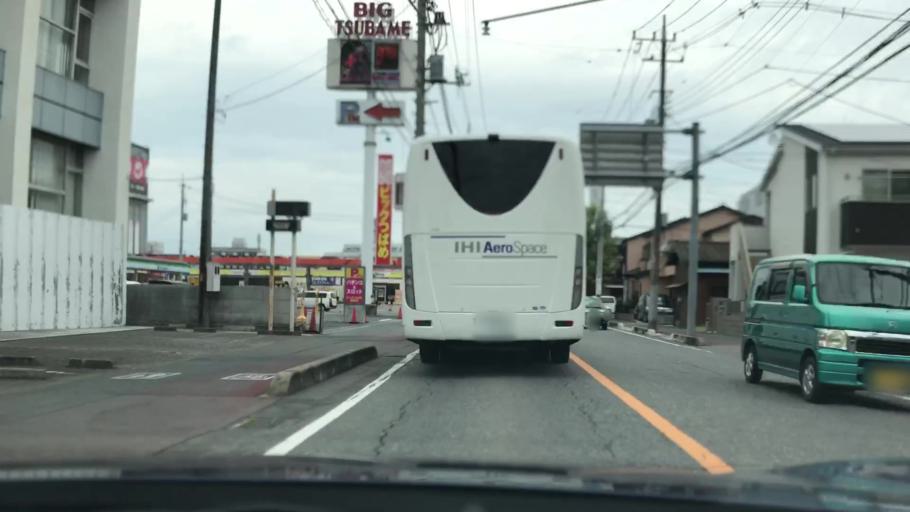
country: JP
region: Gunma
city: Takasaki
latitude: 36.3286
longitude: 139.0144
